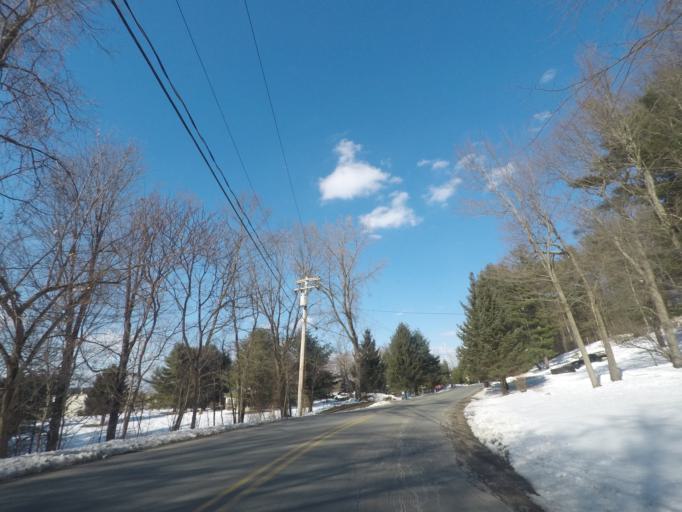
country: US
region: New York
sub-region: Saratoga County
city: Stillwater
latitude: 42.8740
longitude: -73.5822
